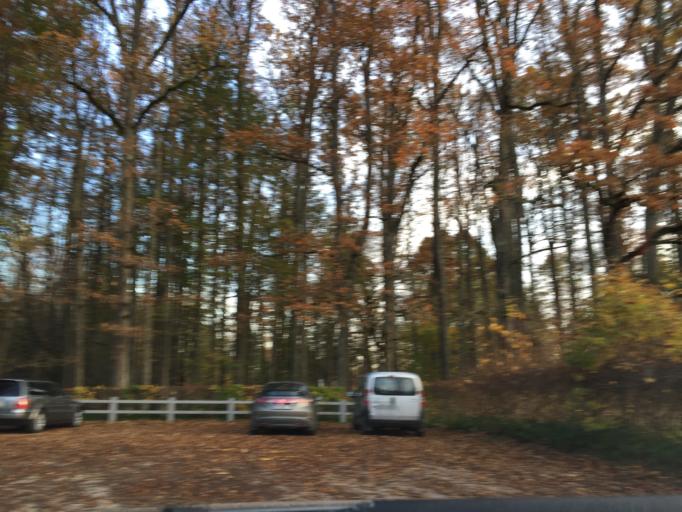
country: LV
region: Jaunjelgava
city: Jaunjelgava
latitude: 56.6173
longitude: 25.0536
